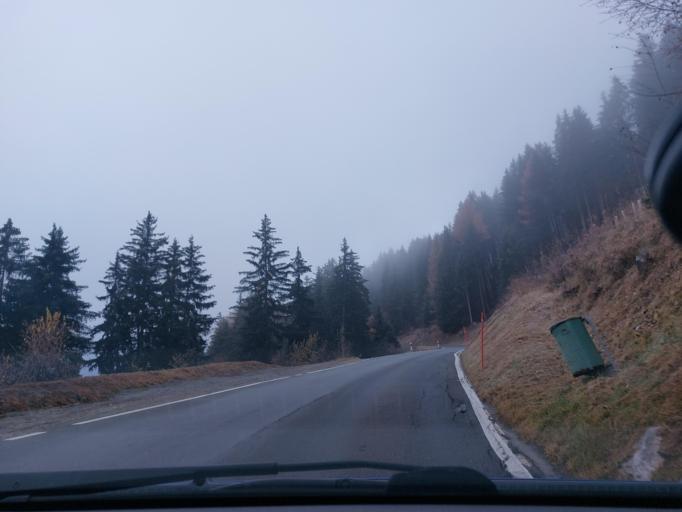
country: CH
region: Valais
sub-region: Conthey District
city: Basse-Nendaz
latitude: 46.1627
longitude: 7.3125
